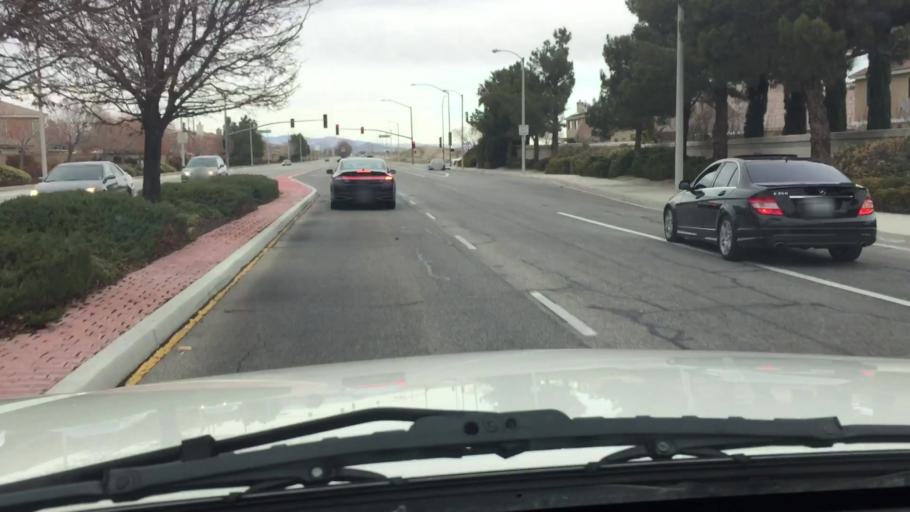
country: US
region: California
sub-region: Los Angeles County
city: Lancaster
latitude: 34.6953
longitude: -118.1838
